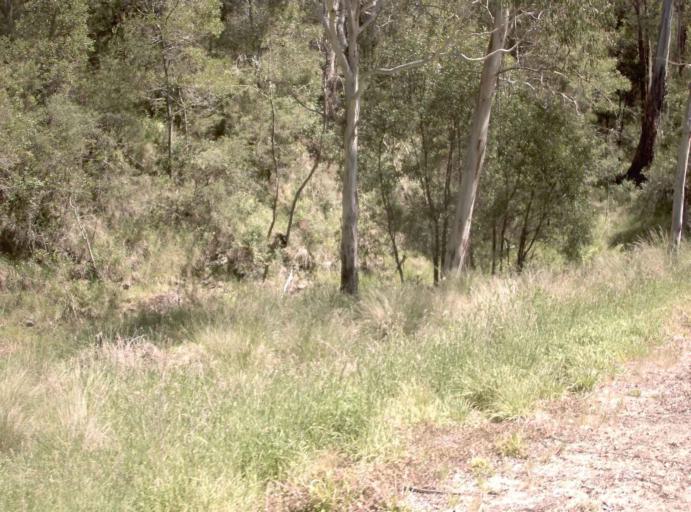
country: AU
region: Victoria
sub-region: East Gippsland
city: Lakes Entrance
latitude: -37.2289
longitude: 148.2632
